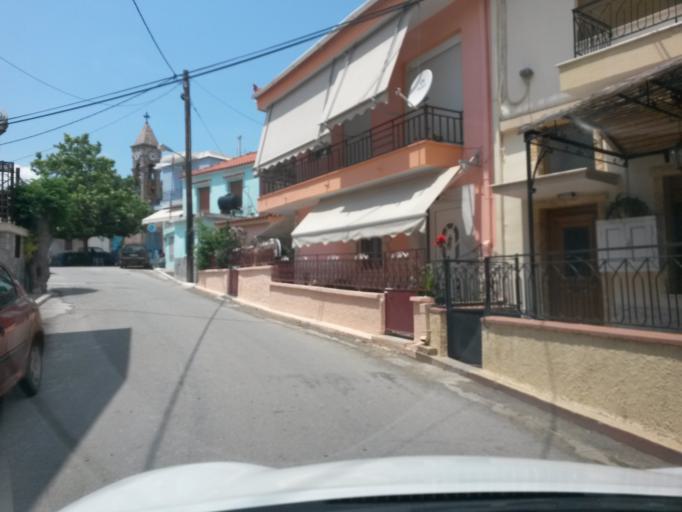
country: GR
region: North Aegean
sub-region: Nomos Lesvou
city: Pamfylla
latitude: 39.1817
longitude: 26.4181
